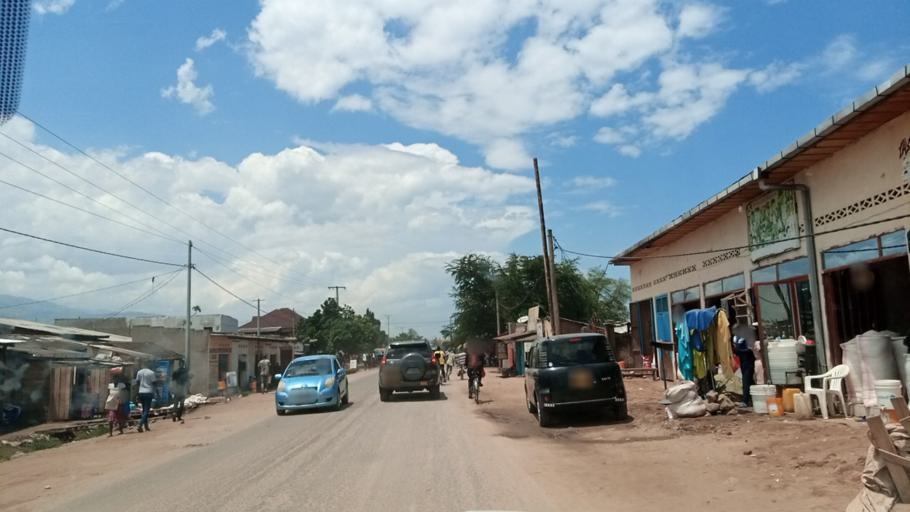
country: BI
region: Bujumbura Mairie
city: Bujumbura
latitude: -3.4289
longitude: 29.3546
